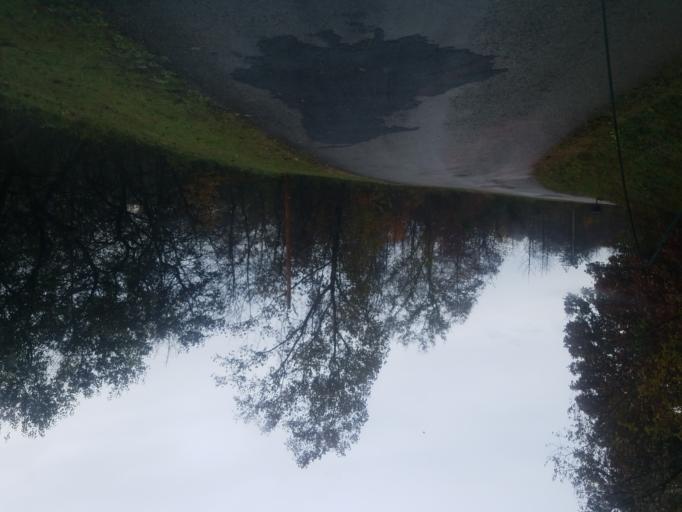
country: US
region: Ohio
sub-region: Morgan County
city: McConnelsville
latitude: 39.5027
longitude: -81.8027
